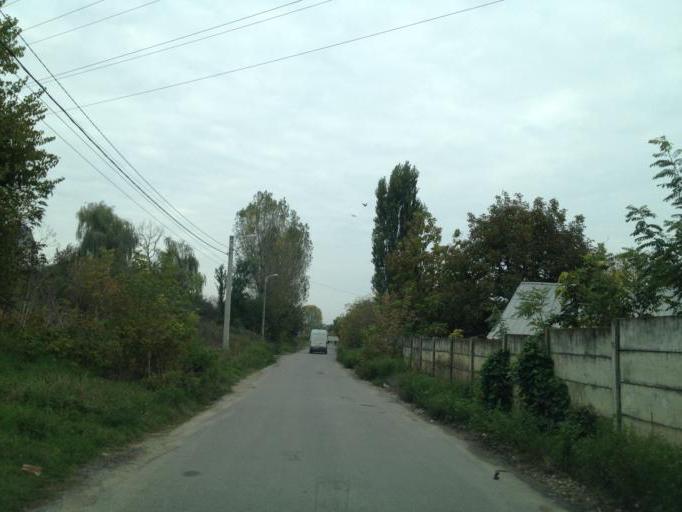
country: RO
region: Dolj
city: Craiova
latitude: 44.2952
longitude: 23.8038
